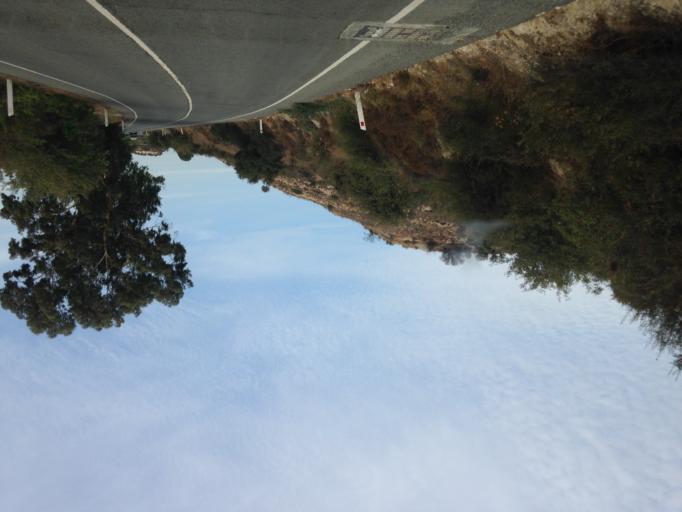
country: CY
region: Limassol
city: Pachna
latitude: 34.8008
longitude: 32.7959
